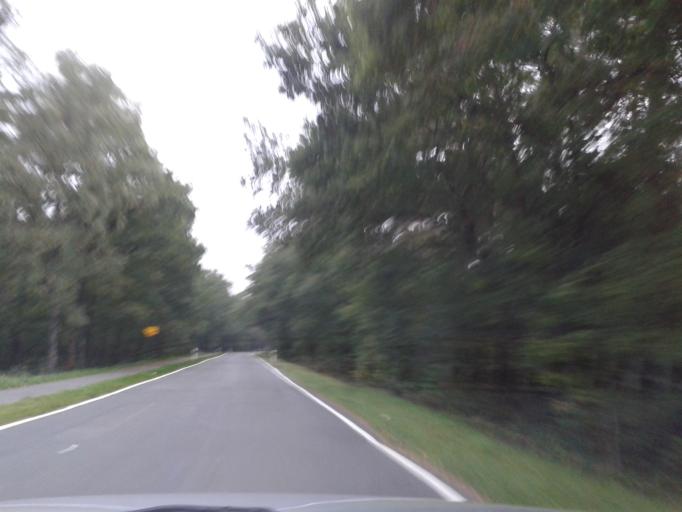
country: DE
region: North Rhine-Westphalia
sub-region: Regierungsbezirk Detmold
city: Augustdorf
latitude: 51.8713
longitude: 8.6872
